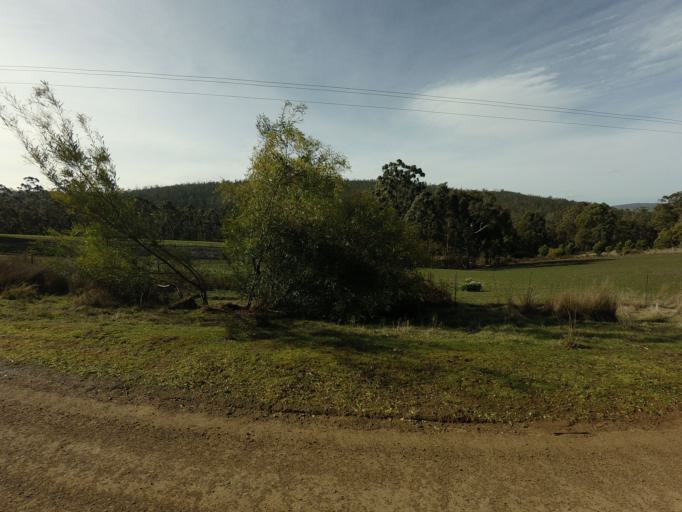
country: AU
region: Tasmania
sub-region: Kingborough
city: Kettering
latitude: -43.0988
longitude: 147.2633
